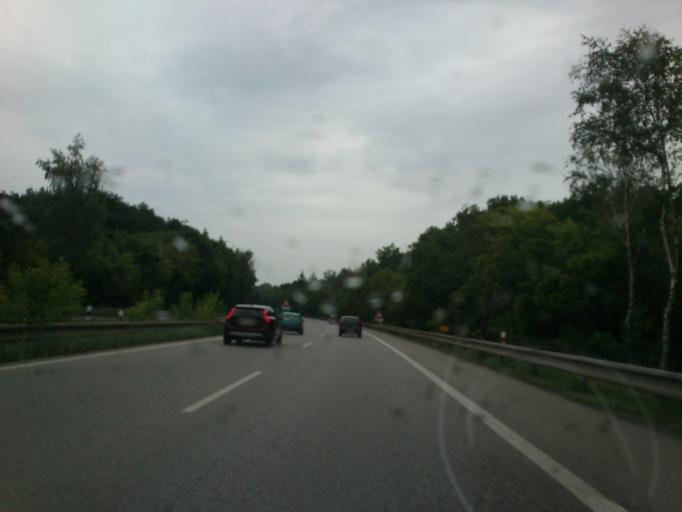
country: CZ
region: Central Bohemia
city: Brandys nad Labem-Stara Boleslav
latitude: 50.1892
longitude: 14.6962
